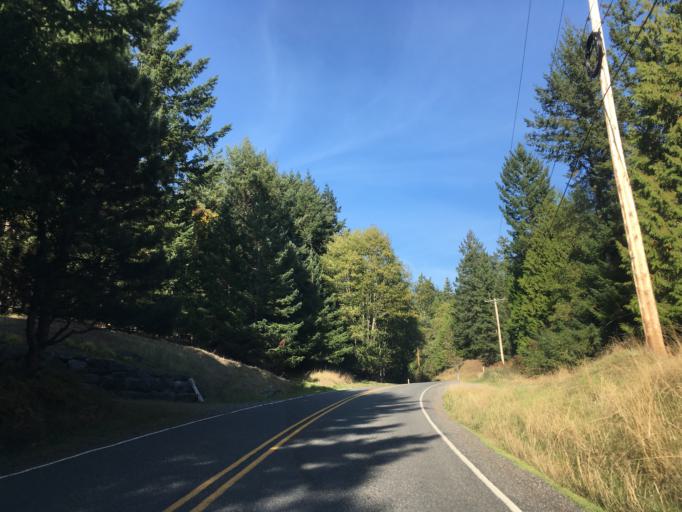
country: US
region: Washington
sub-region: San Juan County
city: Friday Harbor
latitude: 48.6260
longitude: -122.8355
